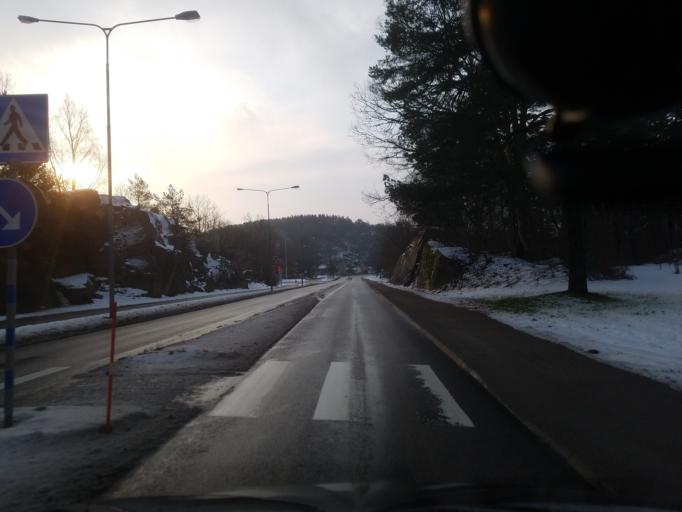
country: SE
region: Vaestra Goetaland
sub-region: Uddevalla Kommun
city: Uddevalla
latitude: 58.3689
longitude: 11.9311
